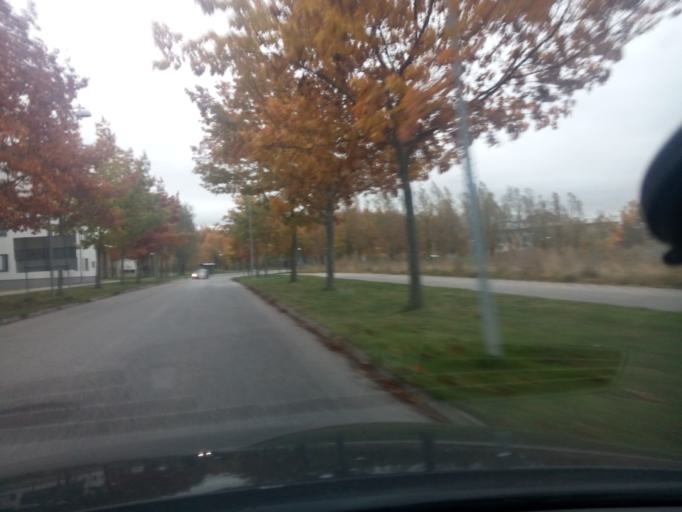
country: SE
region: Soedermanland
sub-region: Nykopings Kommun
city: Nykoping
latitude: 58.7462
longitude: 17.0415
